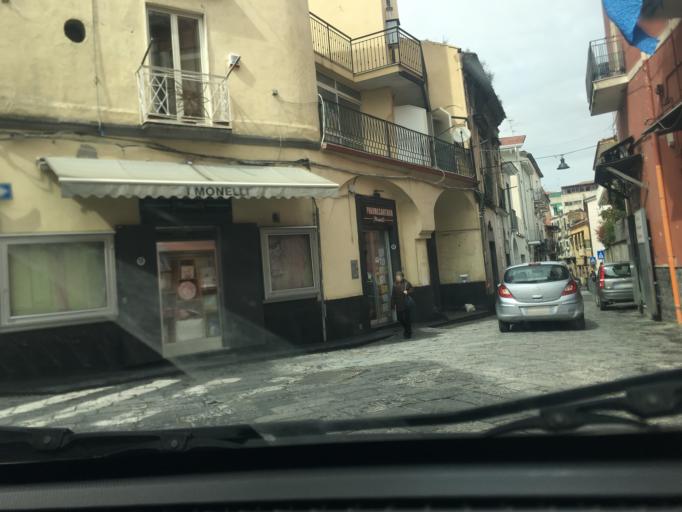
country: IT
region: Campania
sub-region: Provincia di Napoli
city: Marano di Napoli
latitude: 40.8955
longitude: 14.1871
